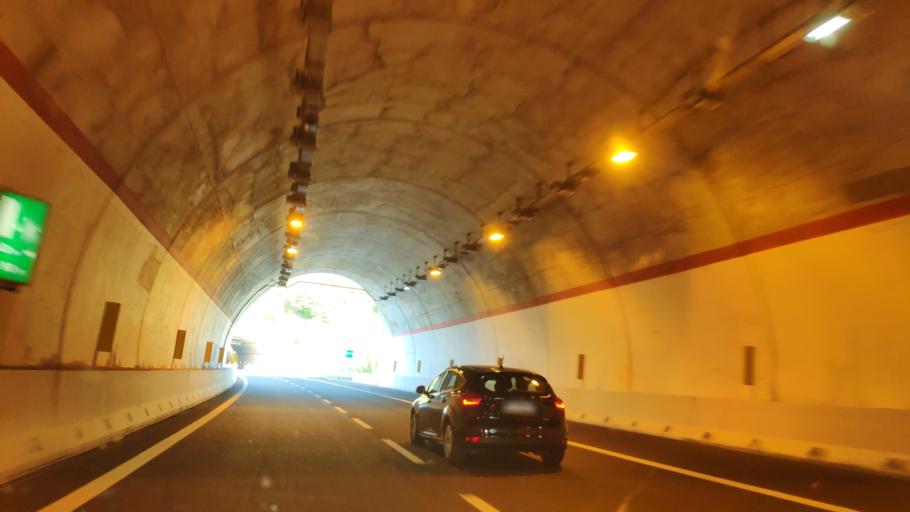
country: IT
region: Basilicate
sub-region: Provincia di Potenza
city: Lagonegro
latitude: 40.1099
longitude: 15.7928
